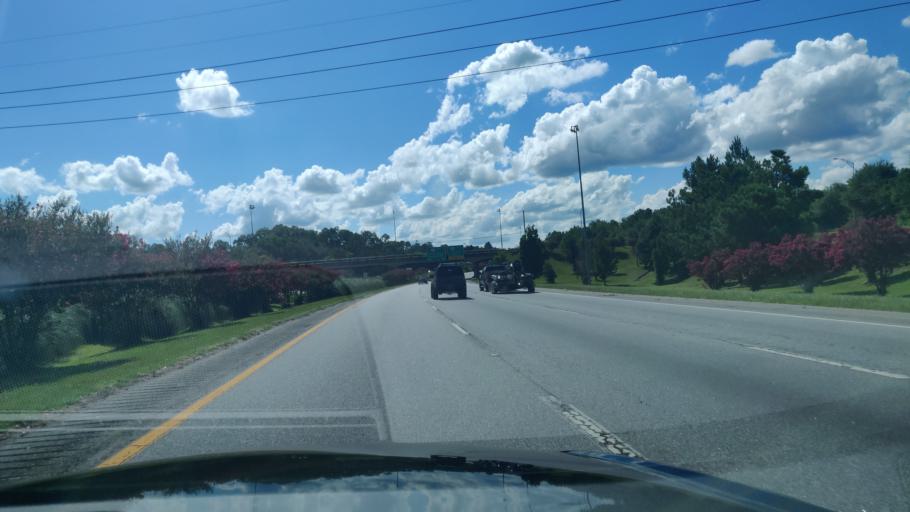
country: US
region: Georgia
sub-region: Muscogee County
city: Columbus
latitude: 32.4531
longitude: -85.0036
